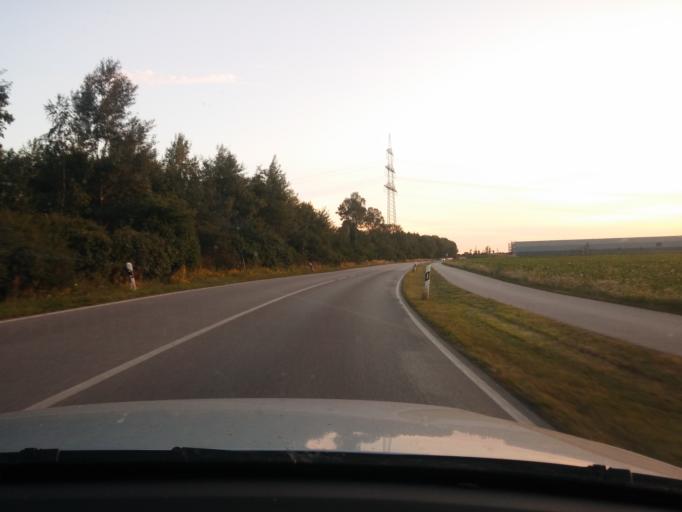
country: DE
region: Bavaria
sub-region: Upper Bavaria
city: Poing
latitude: 48.1626
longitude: 11.7928
